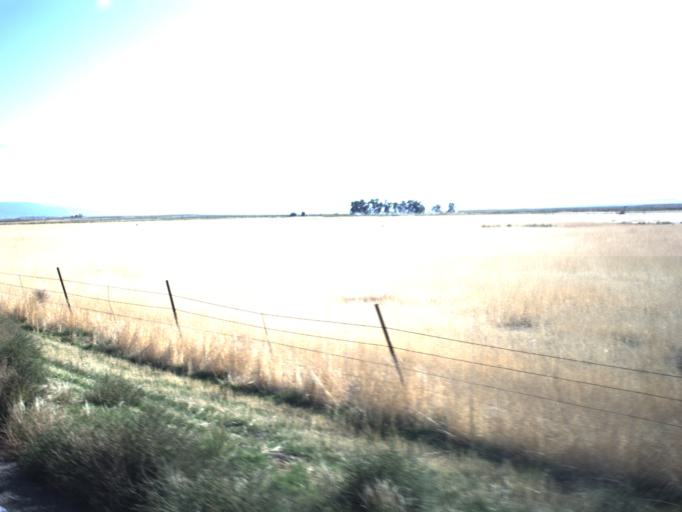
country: US
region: Utah
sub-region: Millard County
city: Delta
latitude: 39.2088
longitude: -112.4133
